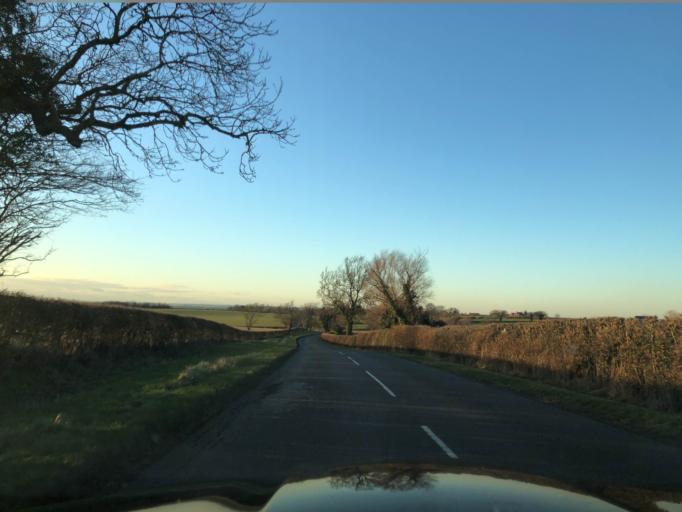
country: GB
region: England
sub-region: Warwickshire
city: Harbury
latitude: 52.2277
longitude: -1.4669
